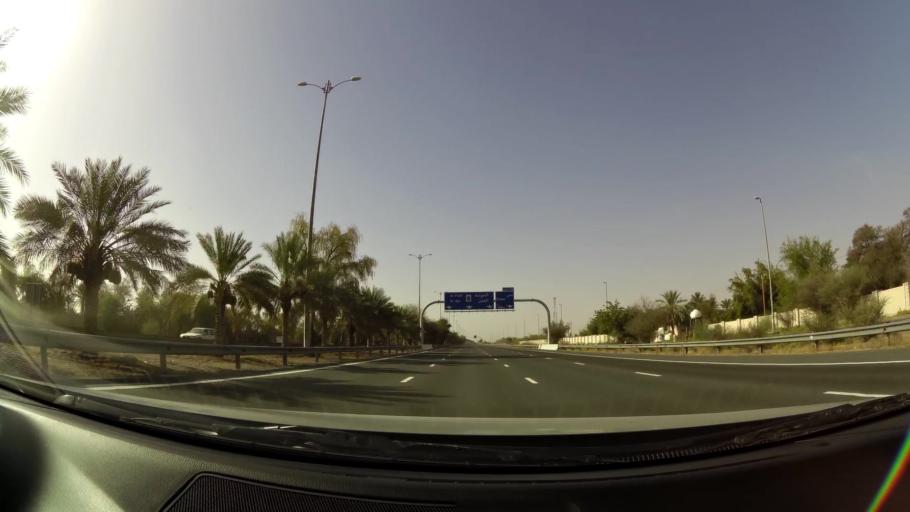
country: OM
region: Al Buraimi
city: Al Buraymi
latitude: 24.4225
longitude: 55.7904
